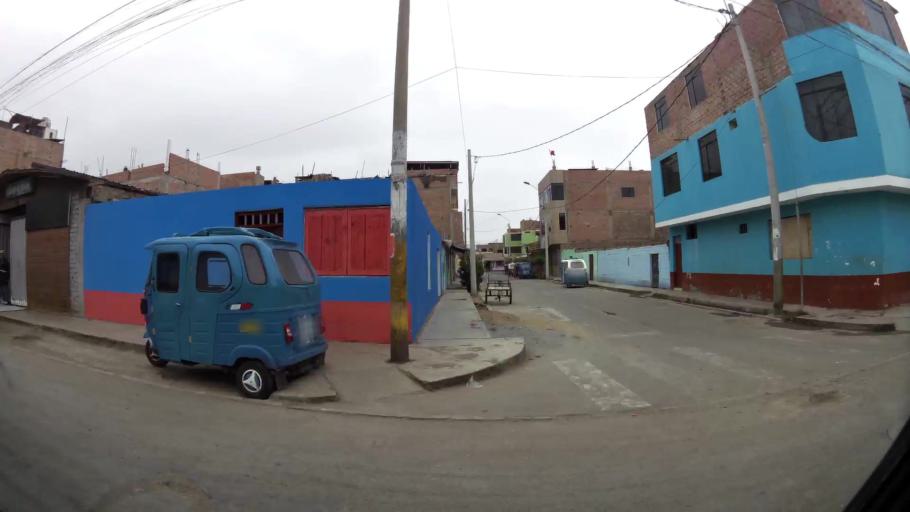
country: PE
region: Lima
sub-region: Barranca
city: Barranca
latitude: -10.7453
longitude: -77.7580
